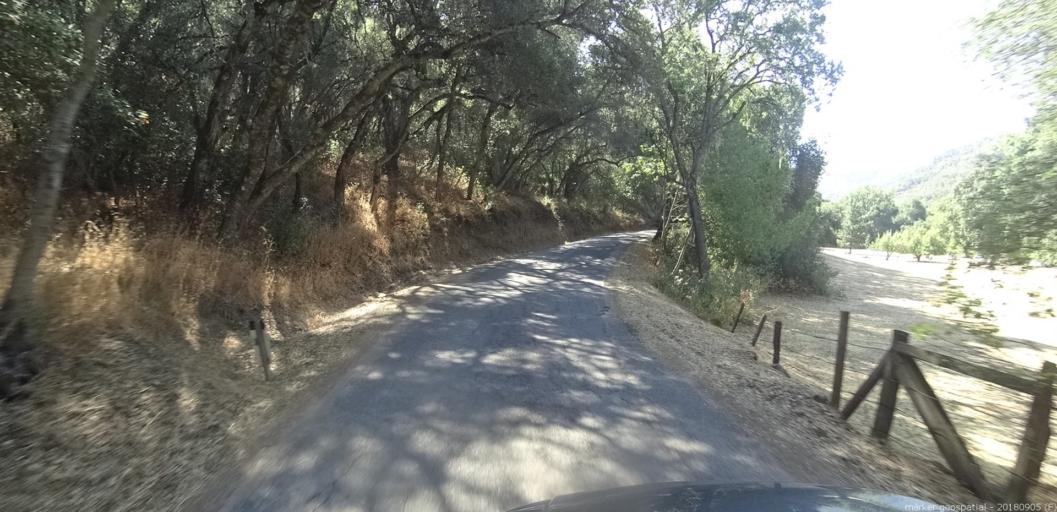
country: US
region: California
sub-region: Monterey County
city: Gonzales
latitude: 36.3746
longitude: -121.5910
